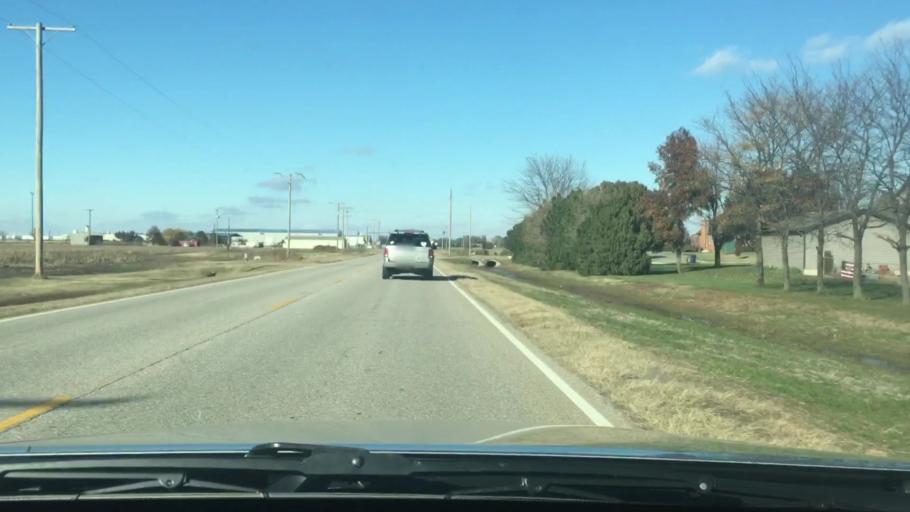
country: US
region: Kansas
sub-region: Sedgwick County
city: Maize
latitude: 37.7772
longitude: -97.4811
